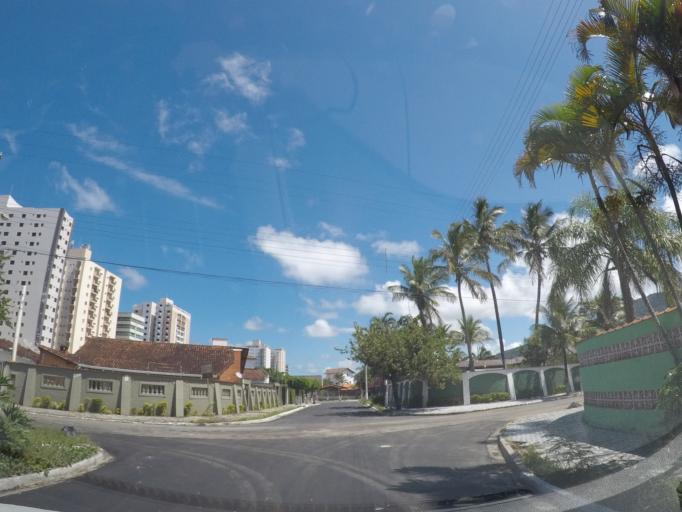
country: BR
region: Sao Paulo
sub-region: Mongagua
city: Mongagua
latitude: -24.0714
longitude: -46.5722
